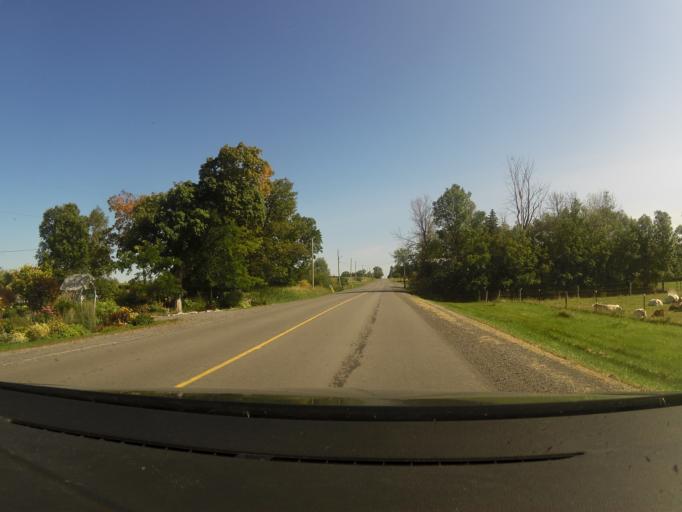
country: CA
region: Ontario
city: Arnprior
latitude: 45.3887
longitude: -76.1378
